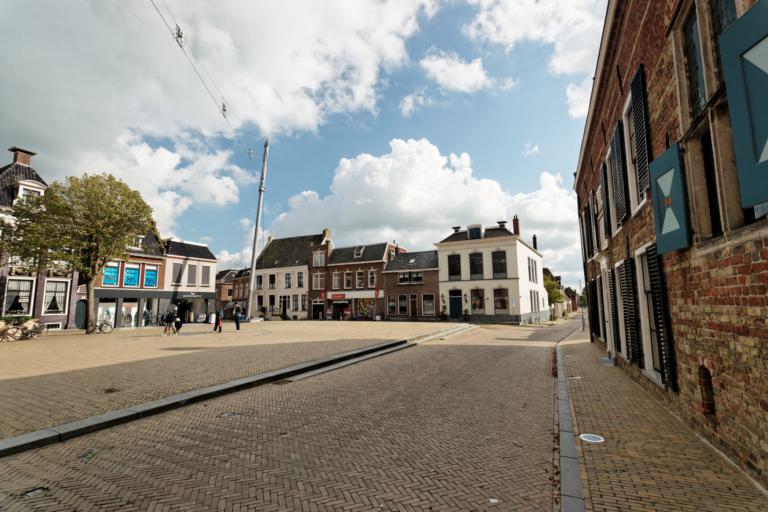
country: NL
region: Friesland
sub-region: Gemeente Franekeradeel
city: Franeker
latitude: 53.1862
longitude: 5.5441
